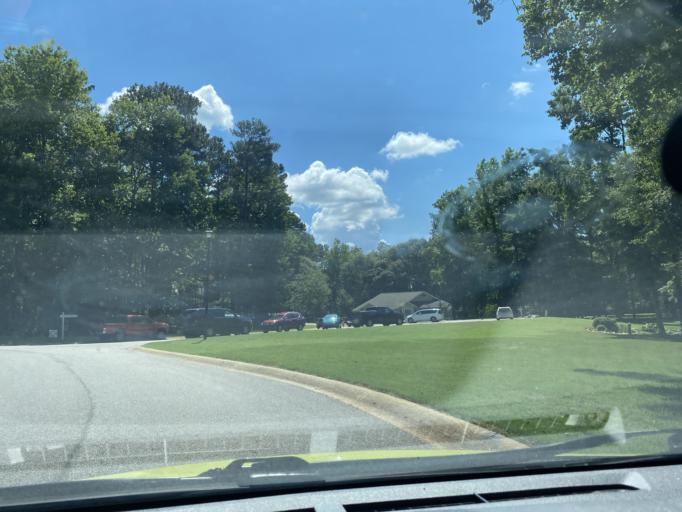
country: US
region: Georgia
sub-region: Fulton County
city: Palmetto
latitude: 33.4315
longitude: -84.6841
